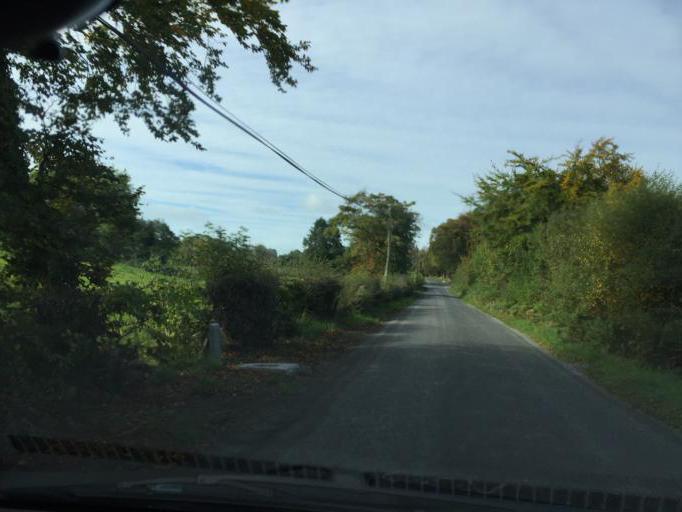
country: IE
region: Connaught
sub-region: Roscommon
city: Boyle
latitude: 54.0299
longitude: -8.2911
